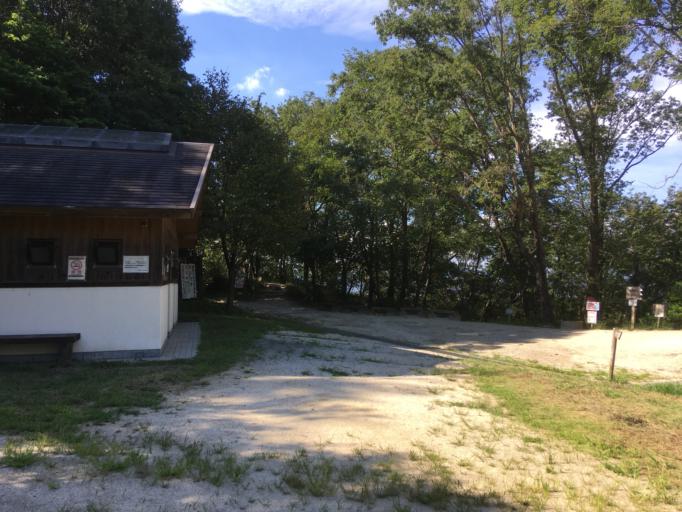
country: JP
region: Osaka
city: Neyagawa
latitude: 34.7495
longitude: 135.6839
